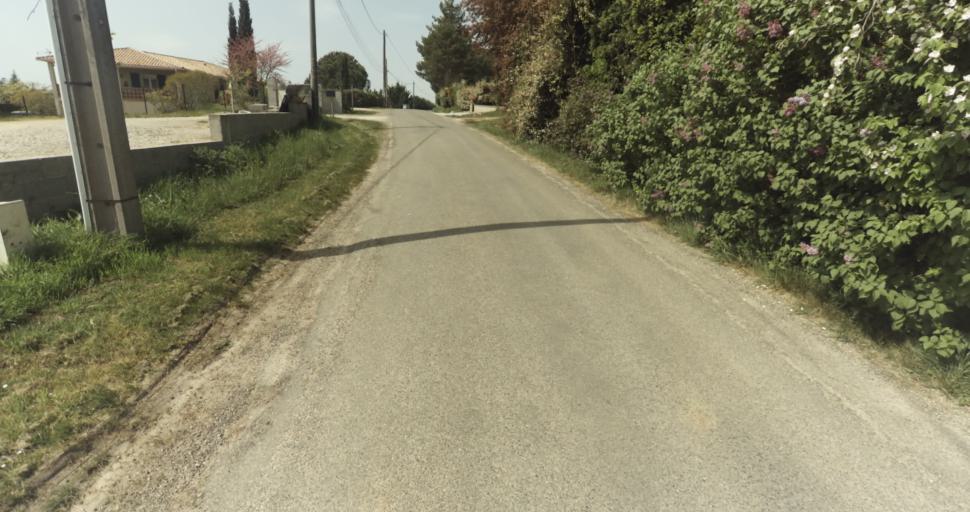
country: FR
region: Midi-Pyrenees
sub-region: Departement du Tarn-et-Garonne
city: Moissac
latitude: 44.1294
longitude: 1.0827
